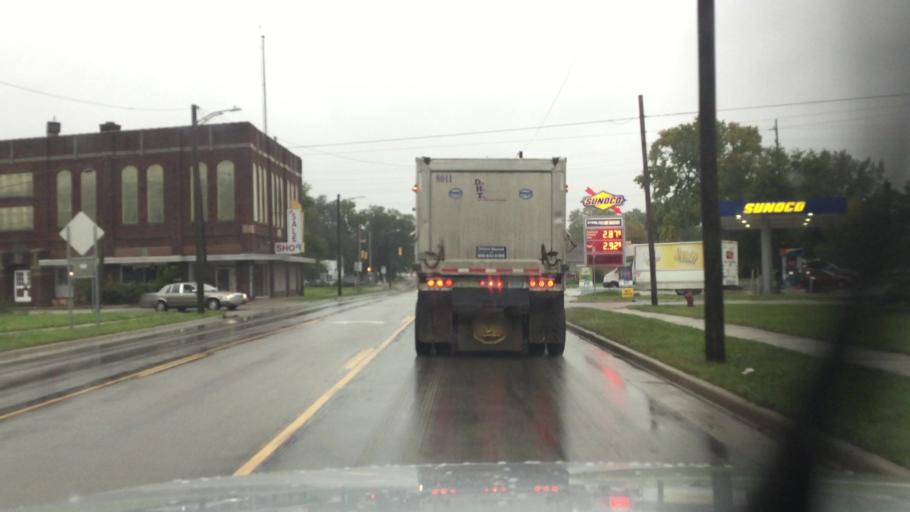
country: US
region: Michigan
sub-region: Saginaw County
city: Saginaw
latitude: 43.4016
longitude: -83.9593
